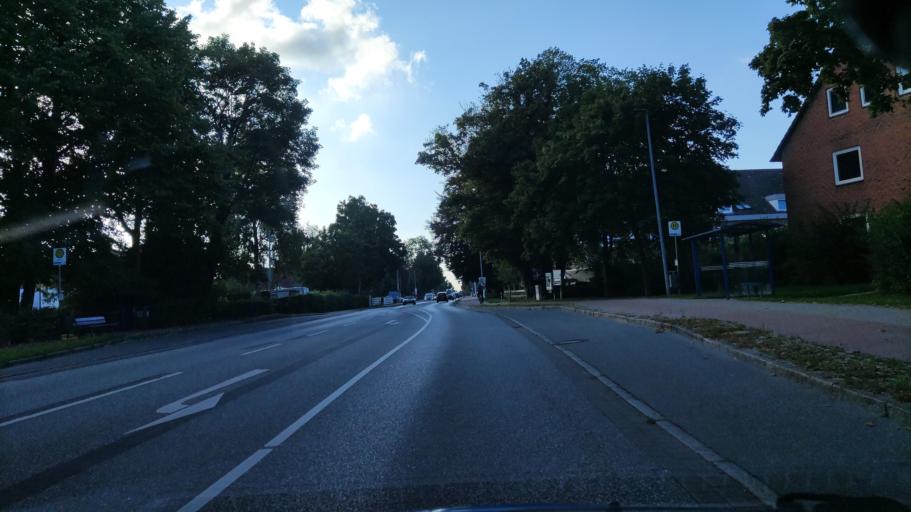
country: DE
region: Schleswig-Holstein
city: Ploen
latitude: 54.1563
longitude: 10.4429
